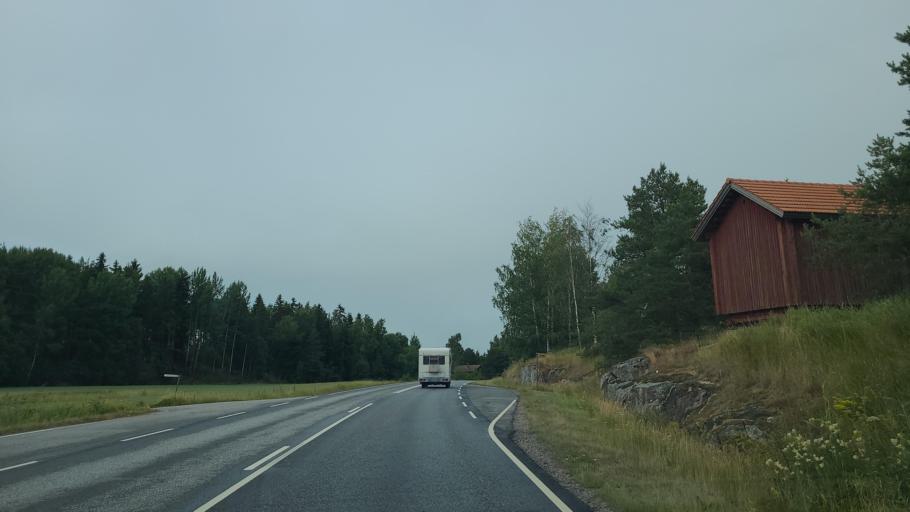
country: FI
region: Varsinais-Suomi
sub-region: Turku
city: Sauvo
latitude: 60.2905
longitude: 22.6725
